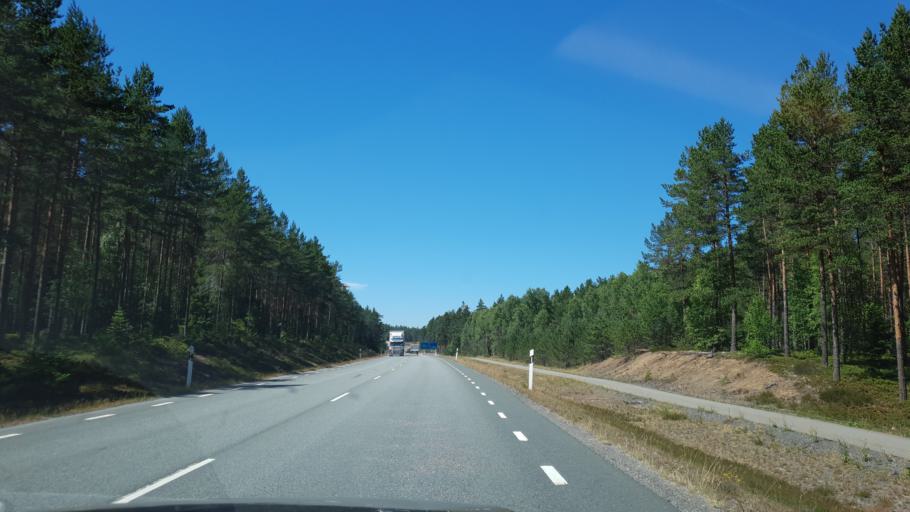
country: SE
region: Joenkoeping
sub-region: Vaggeryds Kommun
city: Vaggeryd
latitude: 57.5257
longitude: 14.1289
